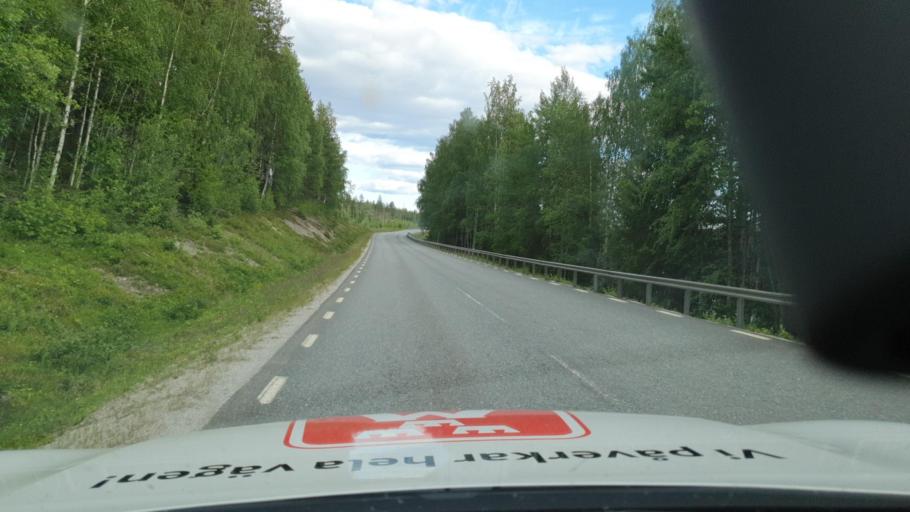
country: SE
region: Vaesterbotten
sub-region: Lycksele Kommun
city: Lycksele
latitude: 64.4175
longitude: 19.0086
